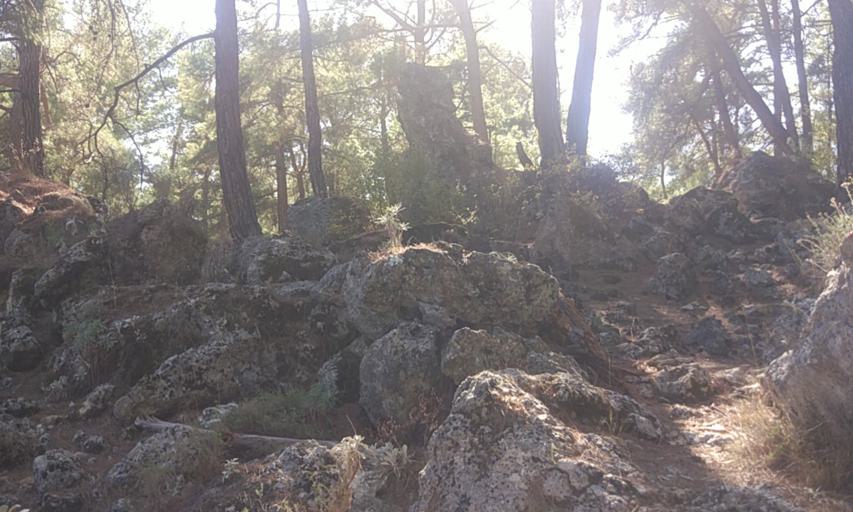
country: TR
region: Antalya
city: Tekirova
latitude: 36.4890
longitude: 30.4276
